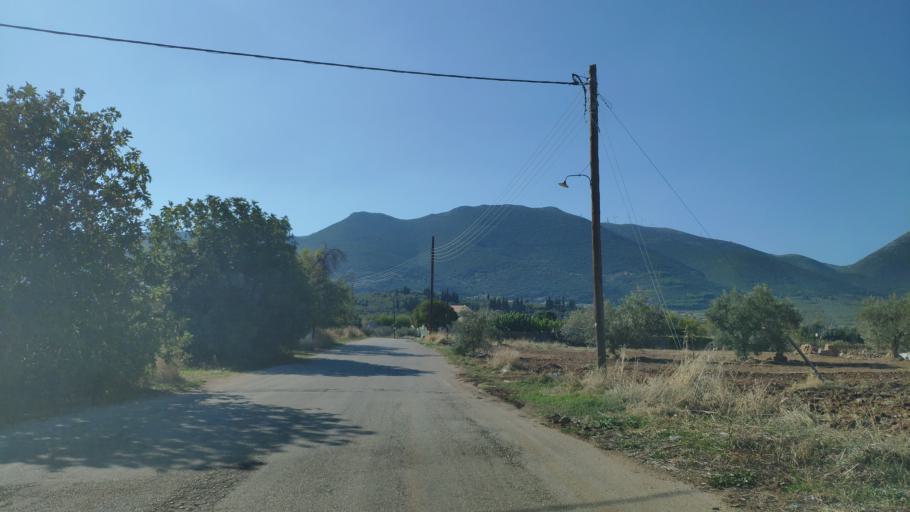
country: GR
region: Peloponnese
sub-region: Nomos Korinthias
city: Khiliomodhi
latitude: 37.8009
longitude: 22.8688
